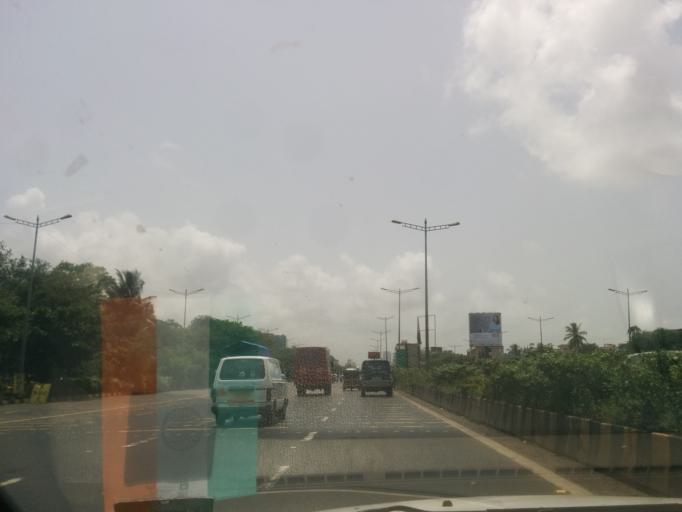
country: IN
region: Maharashtra
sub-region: Mumbai Suburban
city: Mumbai
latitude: 19.0661
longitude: 72.8466
